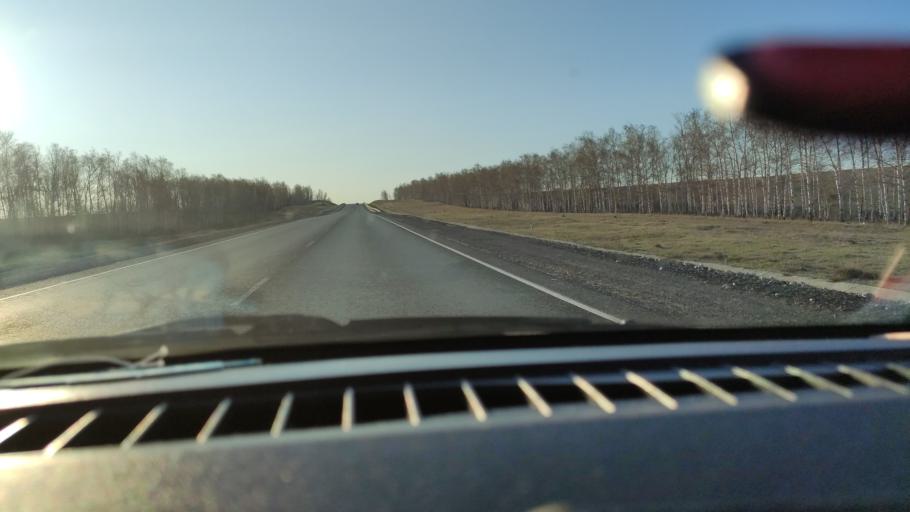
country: RU
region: Saratov
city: Shikhany
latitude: 52.1245
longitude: 47.2483
